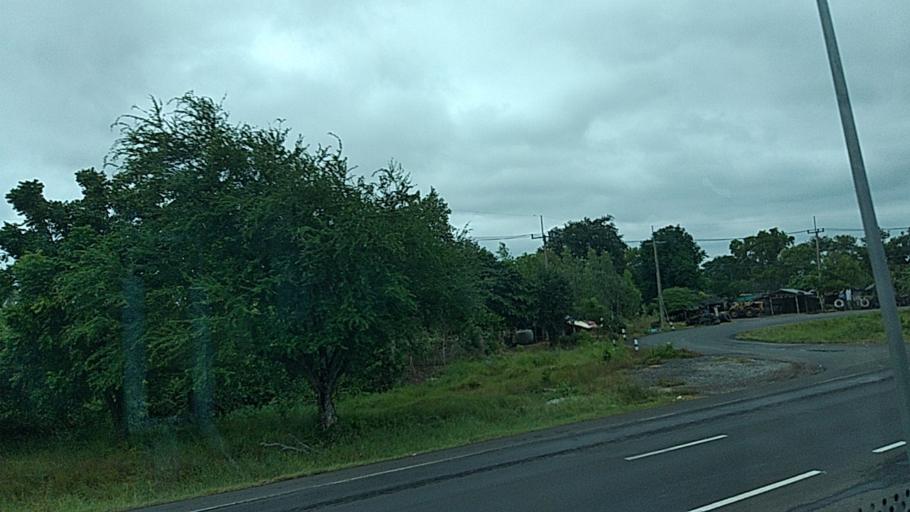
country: TH
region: Nakhon Ratchasima
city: Bua Lai
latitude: 15.6521
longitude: 102.5719
